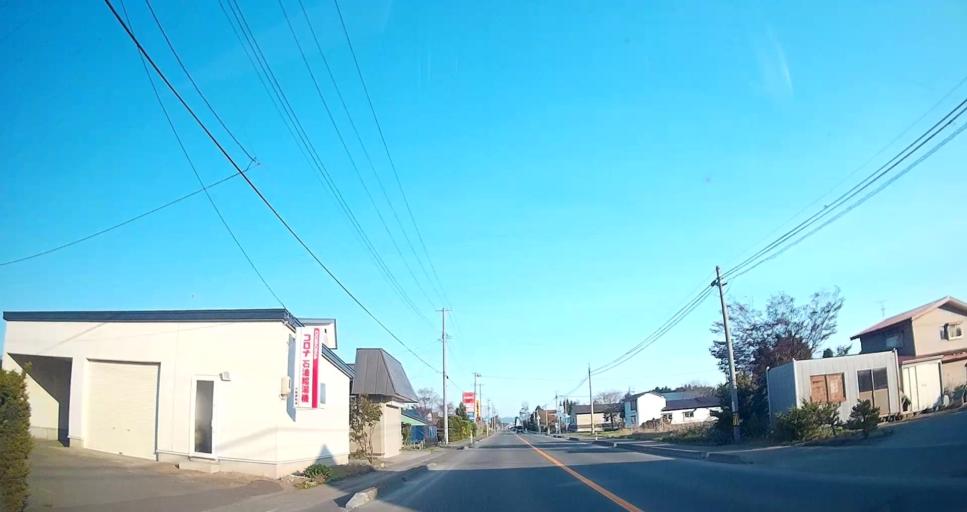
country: JP
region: Aomori
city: Mutsu
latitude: 41.2673
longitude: 141.2210
